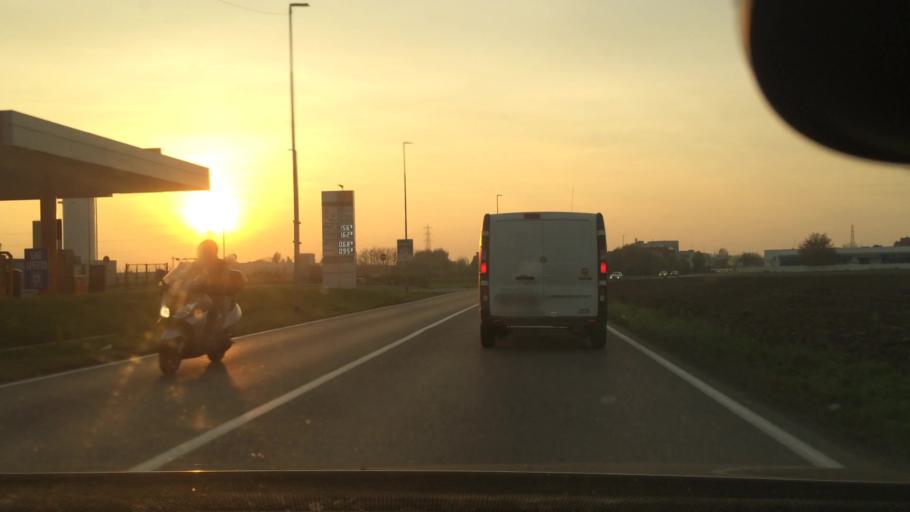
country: IT
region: Lombardy
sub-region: Provincia di Varese
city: Saronno
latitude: 45.6121
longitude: 9.0303
